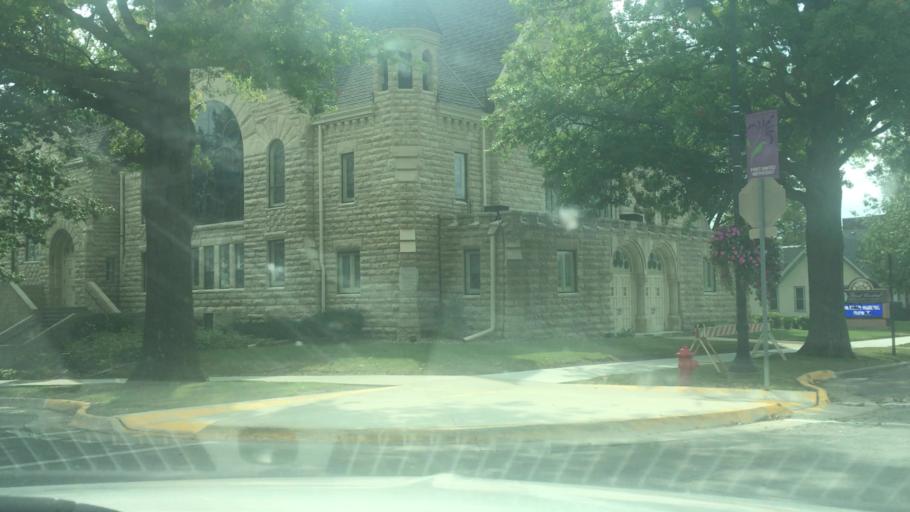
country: US
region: Iowa
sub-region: Marshall County
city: Marshalltown
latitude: 42.0491
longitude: -92.9163
